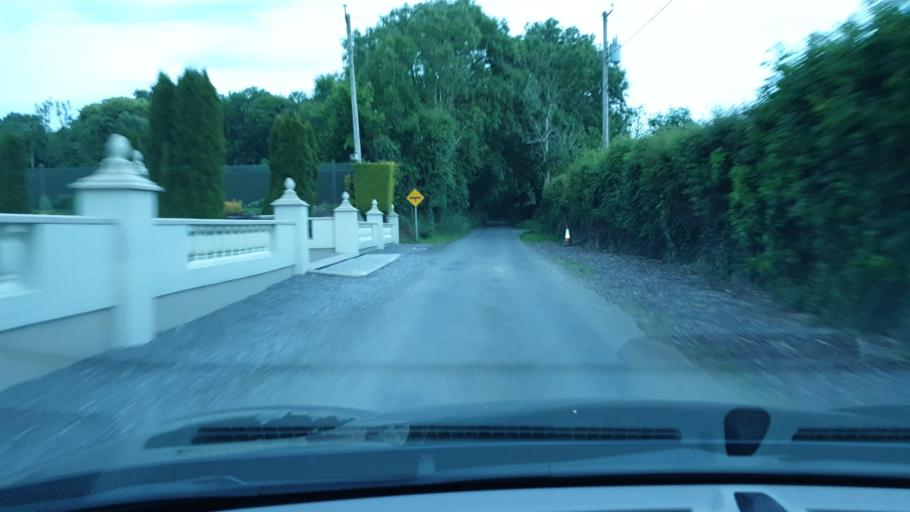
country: IE
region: Leinster
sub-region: An Mhi
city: Duleek
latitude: 53.5910
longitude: -6.3672
